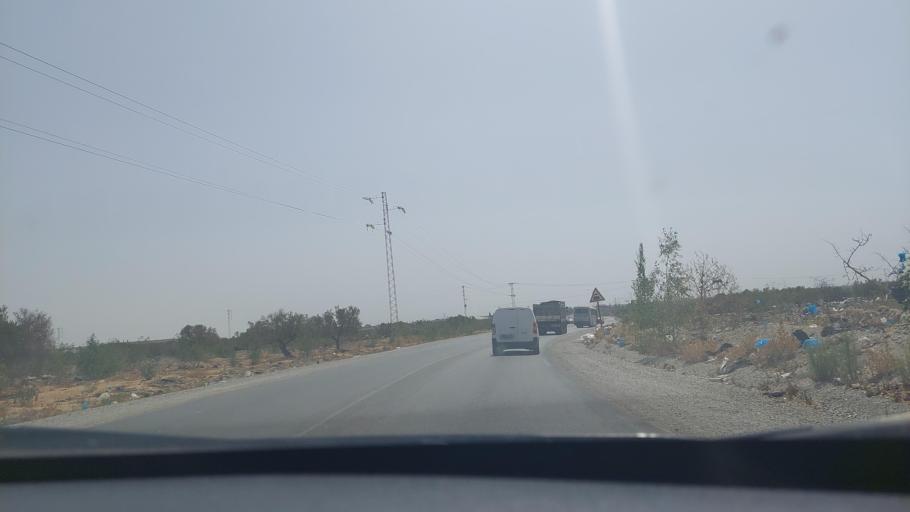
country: TN
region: Al Munastir
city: Qasr Hallal
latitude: 35.6346
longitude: 10.8709
